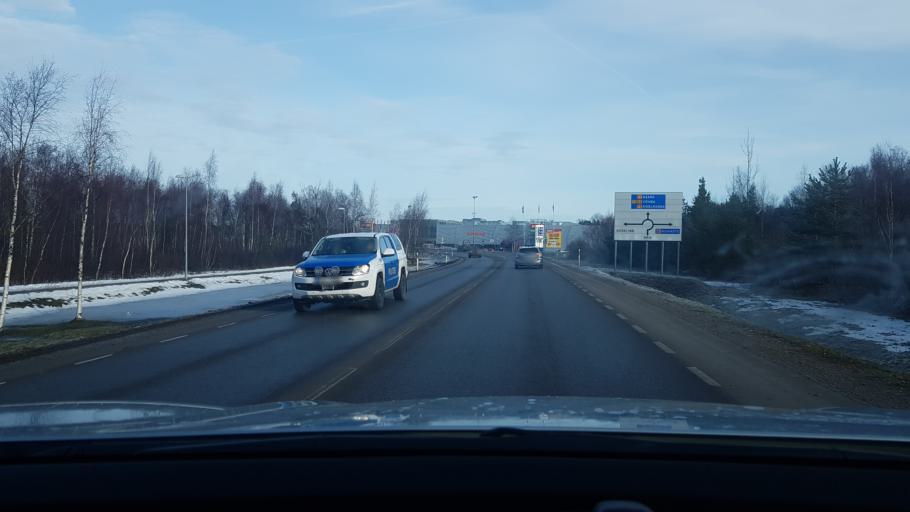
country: EE
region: Saare
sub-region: Kuressaare linn
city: Kuressaare
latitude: 58.2624
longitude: 22.5147
